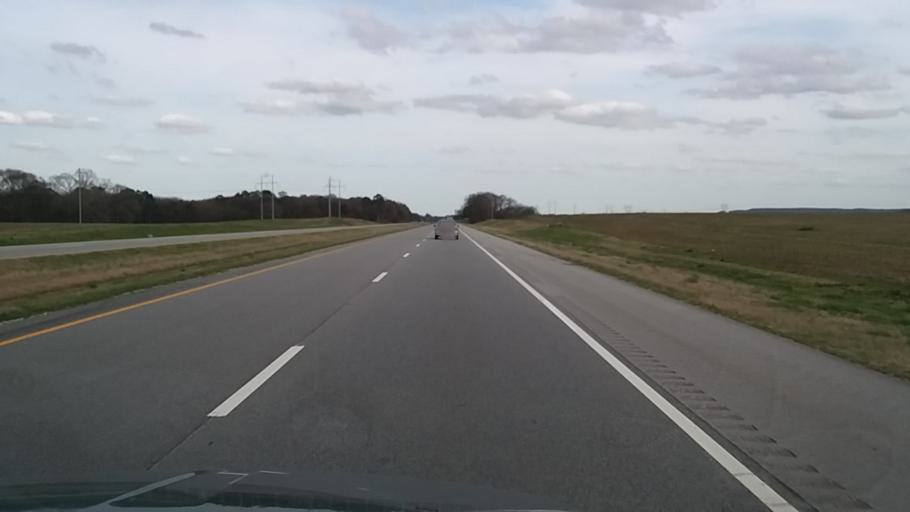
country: US
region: Alabama
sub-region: Lawrence County
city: Town Creek
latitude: 34.6826
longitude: -87.4730
